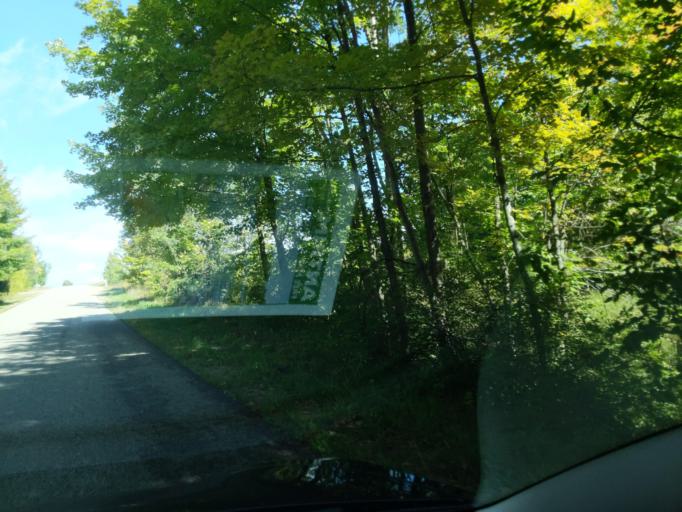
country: US
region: Michigan
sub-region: Antrim County
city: Elk Rapids
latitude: 44.9490
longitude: -85.3323
